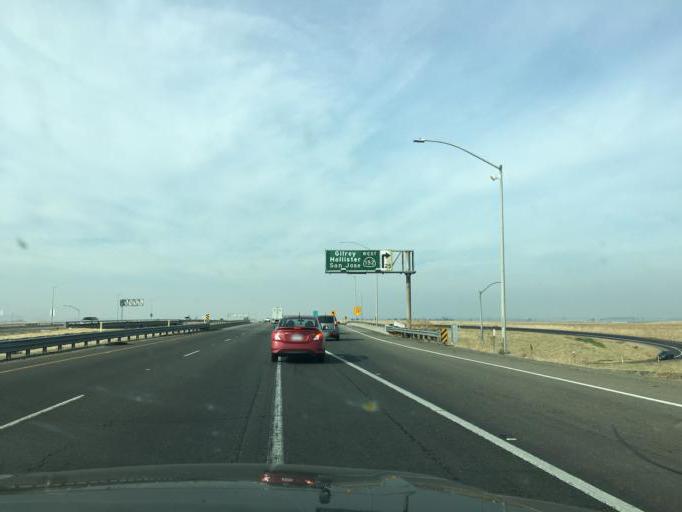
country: US
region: California
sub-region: Merced County
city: Los Banos
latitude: 37.0558
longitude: -120.9686
